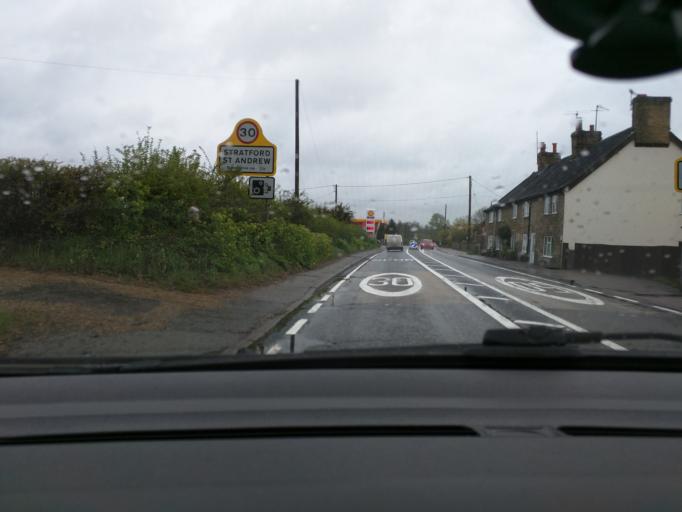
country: GB
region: England
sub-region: Suffolk
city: Saxmundham
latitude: 52.1875
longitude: 1.4471
